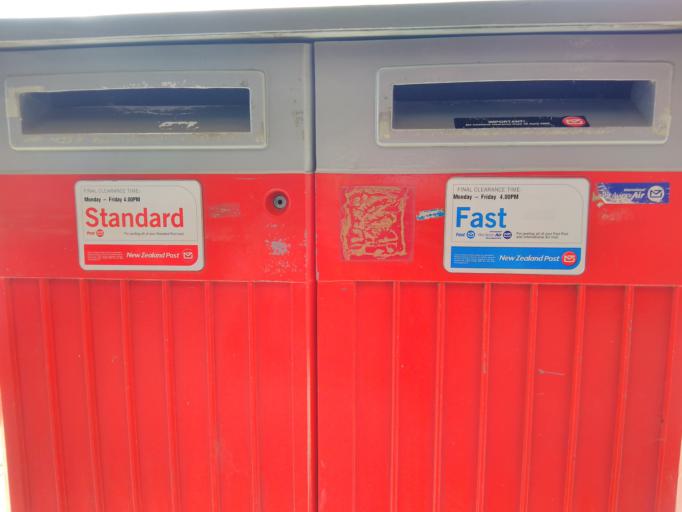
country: NZ
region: Northland
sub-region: Far North District
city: Paihia
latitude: -35.2825
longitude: 174.0909
